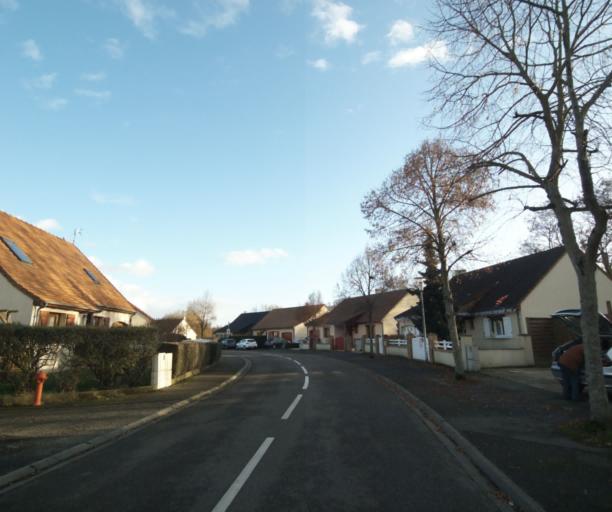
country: FR
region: Pays de la Loire
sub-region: Departement de la Sarthe
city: Allonnes
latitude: 47.9860
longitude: 0.1694
